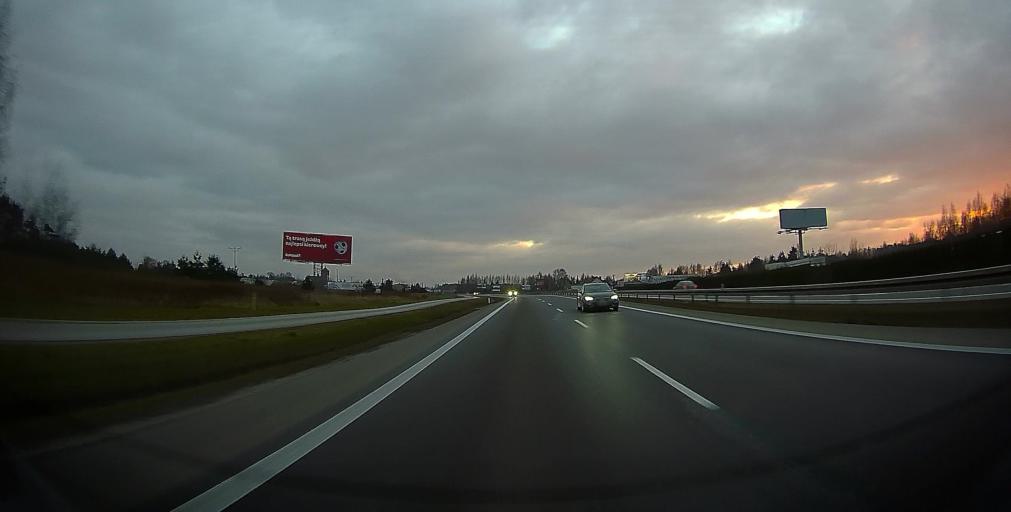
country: PL
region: Masovian Voivodeship
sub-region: Powiat radomski
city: Jedlinsk
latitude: 51.4925
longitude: 21.1196
